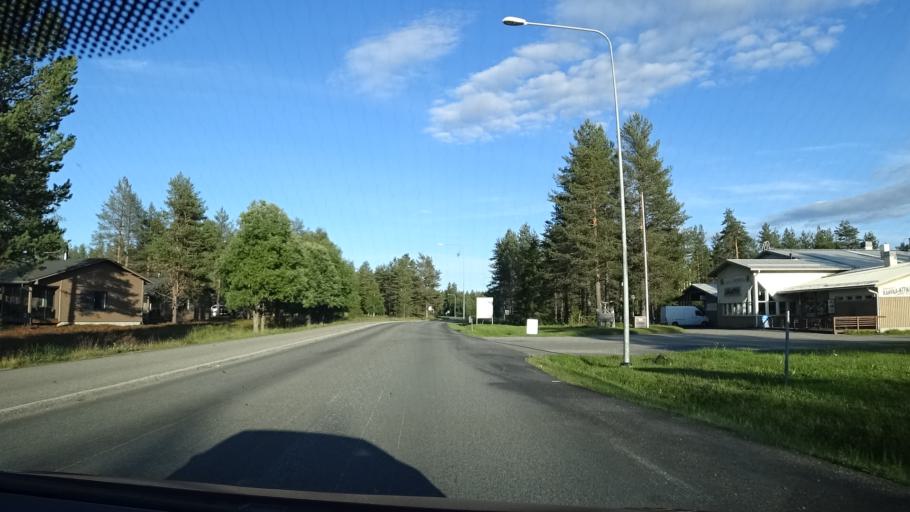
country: FI
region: Northern Ostrobothnia
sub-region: Koillismaa
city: Kuusamo
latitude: 65.9994
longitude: 29.1573
